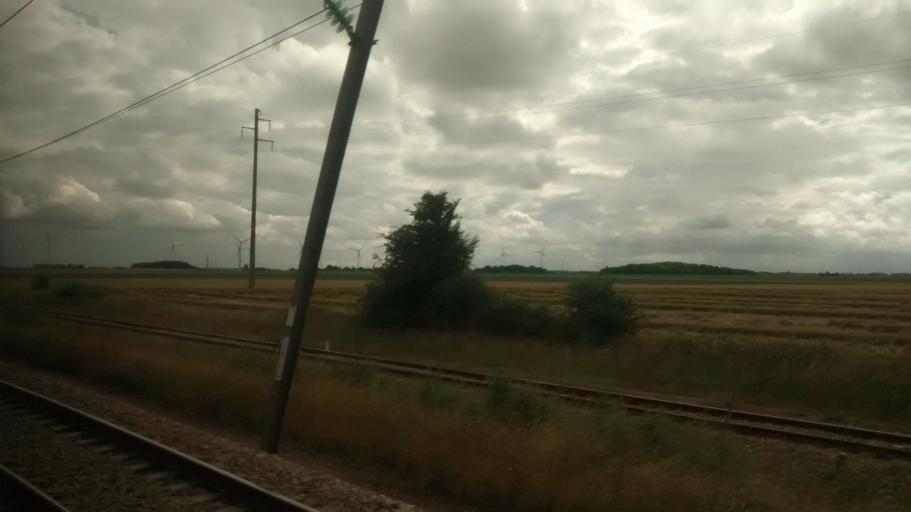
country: FR
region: Centre
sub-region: Departement d'Eure-et-Loir
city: Voves
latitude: 48.3390
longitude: 1.6809
